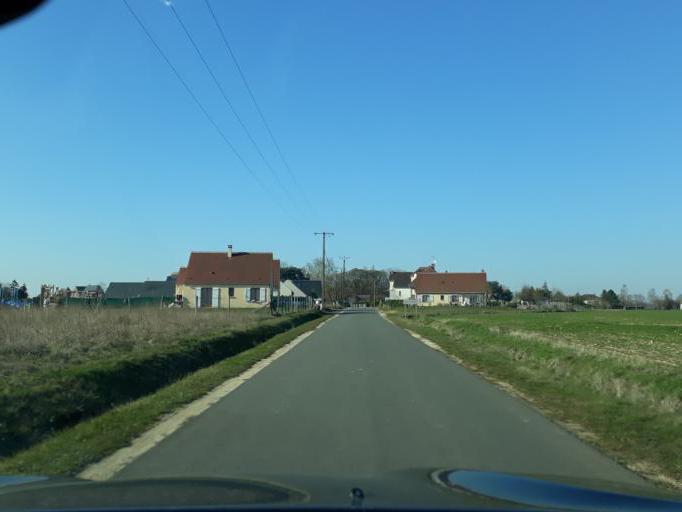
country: FR
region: Centre
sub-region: Departement du Loir-et-Cher
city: Oucques
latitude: 47.8204
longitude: 1.4008
